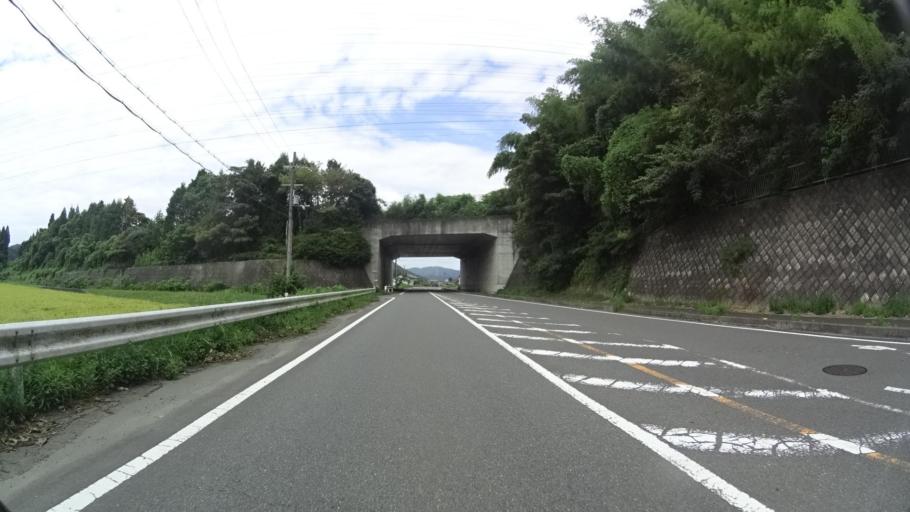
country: JP
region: Kyoto
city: Ayabe
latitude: 35.3231
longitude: 135.2142
